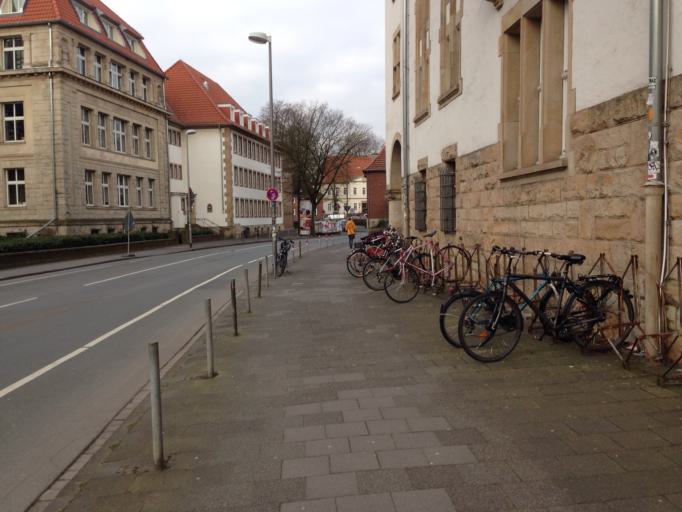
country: DE
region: North Rhine-Westphalia
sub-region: Regierungsbezirk Munster
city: Muenster
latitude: 51.9608
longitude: 7.6214
